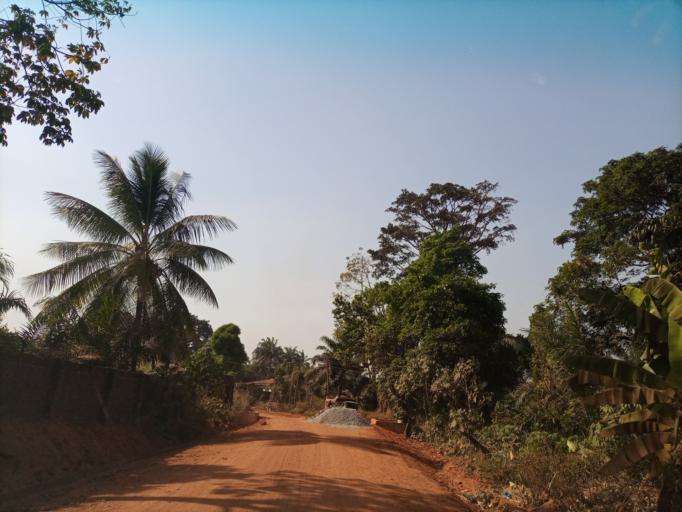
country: NG
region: Enugu
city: Aku
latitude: 6.7055
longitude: 7.3123
